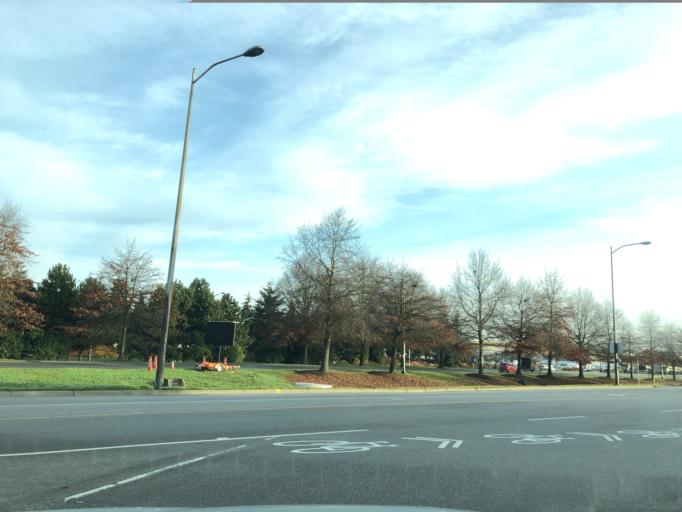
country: CA
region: British Columbia
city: Richmond
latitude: 49.1919
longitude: -123.1696
